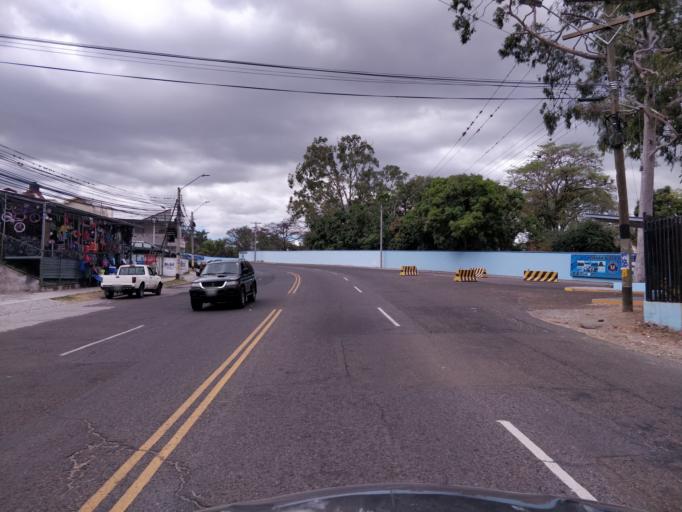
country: HN
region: Francisco Morazan
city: Tegucigalpa
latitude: 14.0510
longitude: -87.2166
